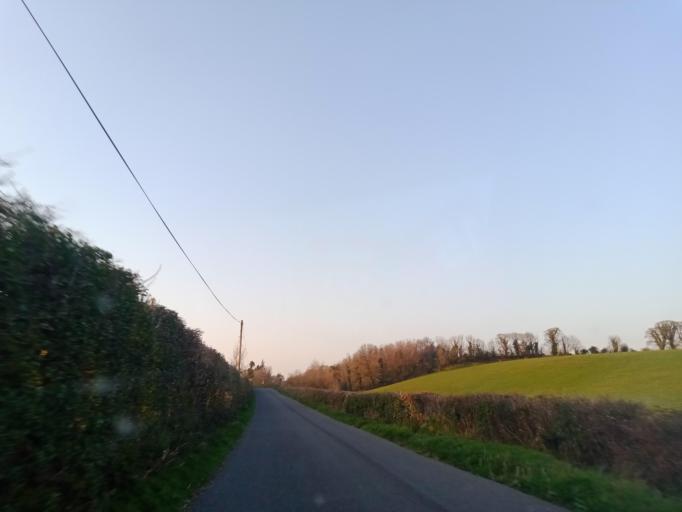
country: IE
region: Leinster
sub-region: Kilkenny
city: Kilkenny
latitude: 52.7276
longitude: -7.2367
